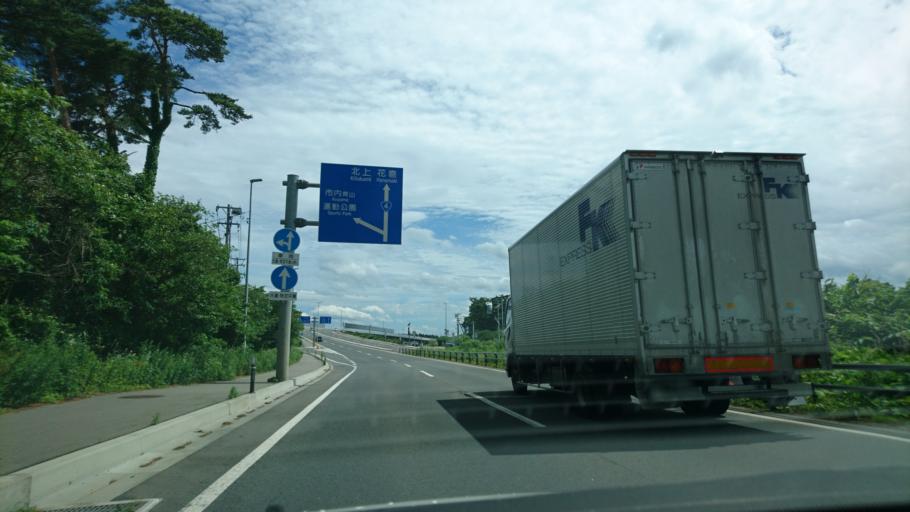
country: JP
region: Iwate
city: Morioka-shi
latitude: 39.7592
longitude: 141.1341
